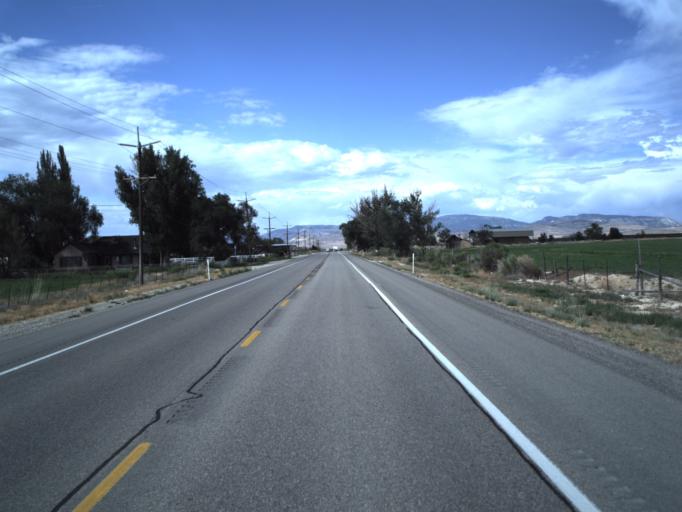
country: US
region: Utah
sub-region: Sanpete County
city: Centerfield
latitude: 39.0898
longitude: -111.8200
